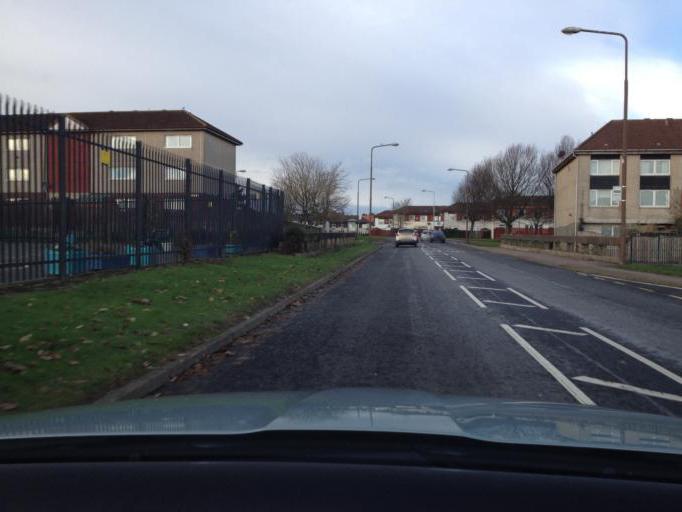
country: GB
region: Scotland
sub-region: West Lothian
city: Mid Calder
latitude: 55.8989
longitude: -3.4897
